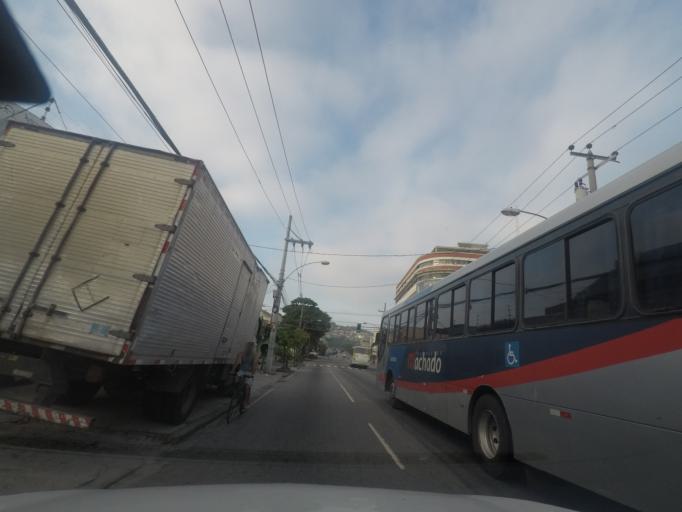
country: BR
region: Rio de Janeiro
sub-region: Duque De Caxias
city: Duque de Caxias
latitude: -22.8340
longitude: -43.2811
